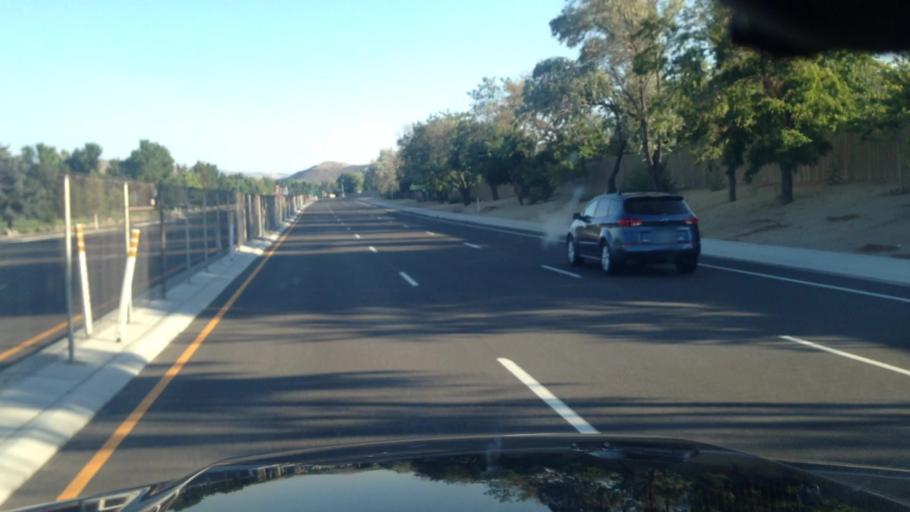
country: US
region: Nevada
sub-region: Washoe County
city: Sparks
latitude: 39.4919
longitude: -119.7481
